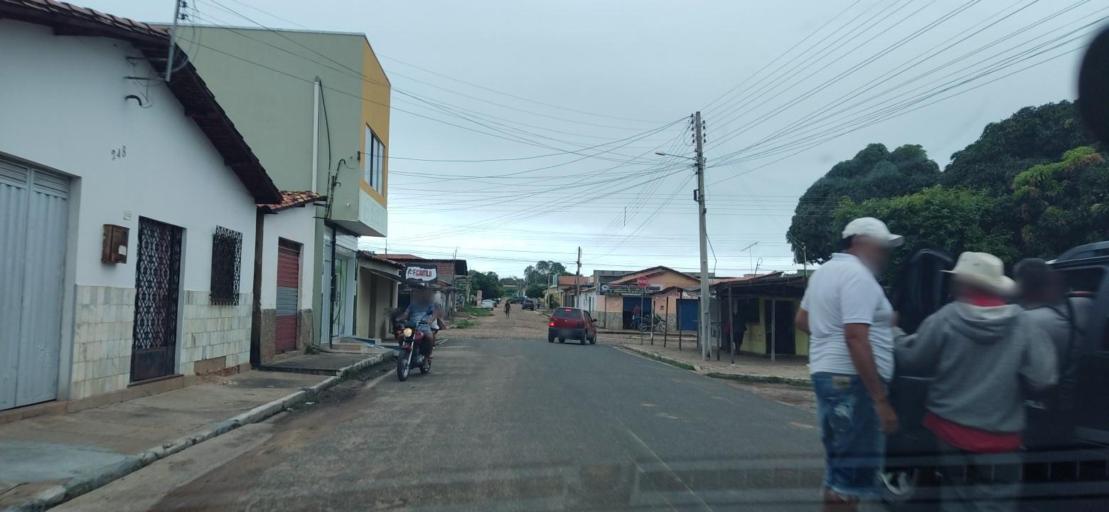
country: BR
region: Piaui
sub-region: Valenca Do Piaui
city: Valenca do Piaui
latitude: -6.4060
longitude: -41.7380
